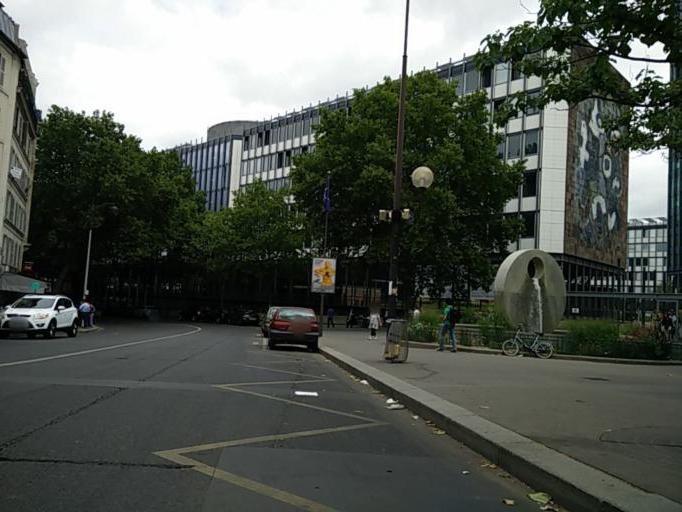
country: FR
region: Ile-de-France
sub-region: Paris
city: Paris
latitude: 48.8461
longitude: 2.3546
